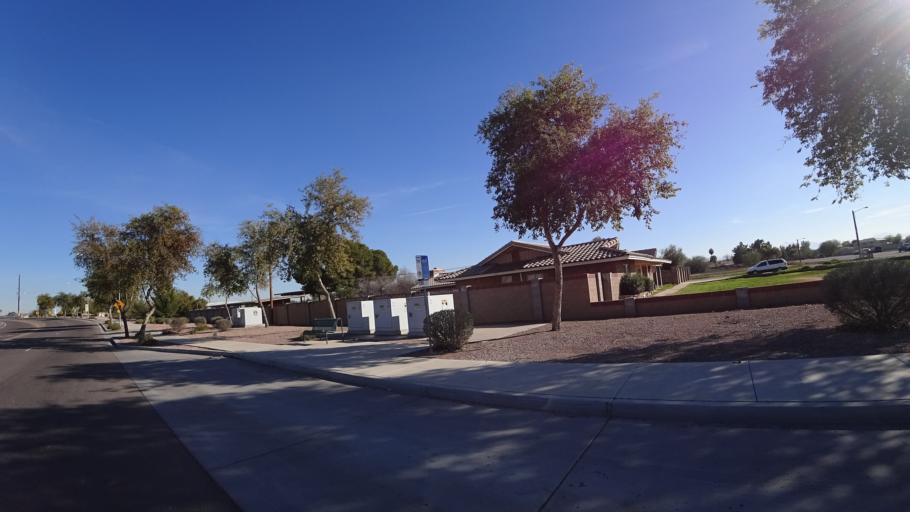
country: US
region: Arizona
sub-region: Maricopa County
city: Glendale
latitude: 33.5223
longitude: -112.2373
